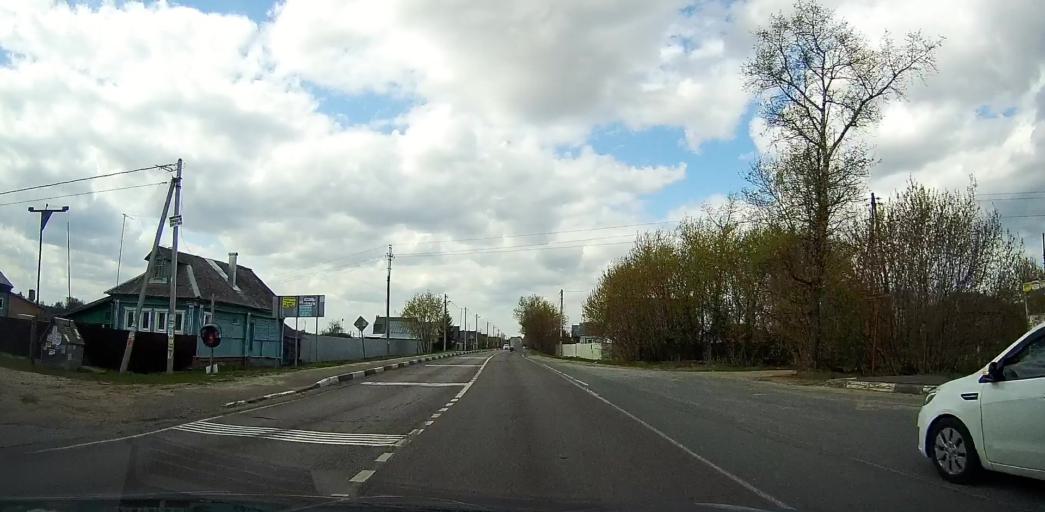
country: RU
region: Moskovskaya
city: Davydovo
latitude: 55.6369
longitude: 38.8679
